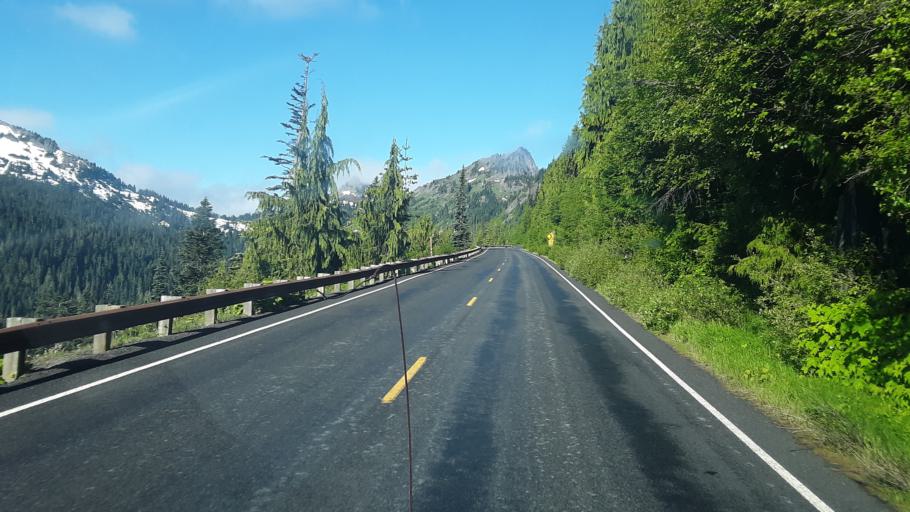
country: US
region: Washington
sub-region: King County
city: Enumclaw
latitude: 46.8911
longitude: -121.4901
